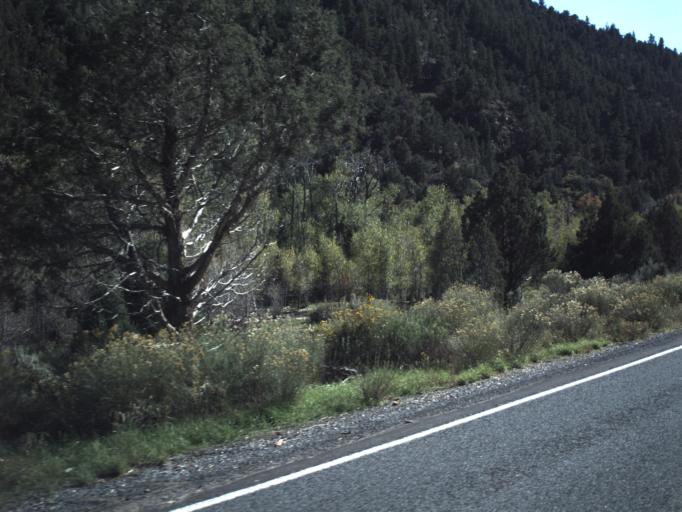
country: US
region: Utah
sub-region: Iron County
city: Parowan
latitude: 37.7932
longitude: -112.8193
